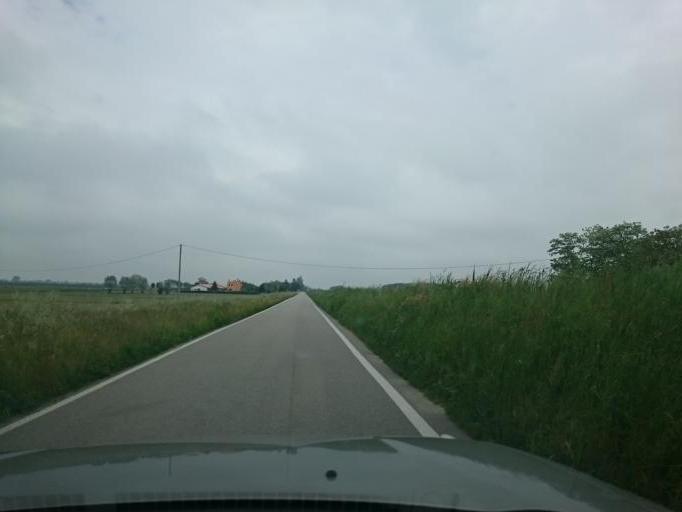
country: IT
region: Veneto
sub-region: Provincia di Venezia
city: Valli
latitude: 45.2113
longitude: 12.1358
